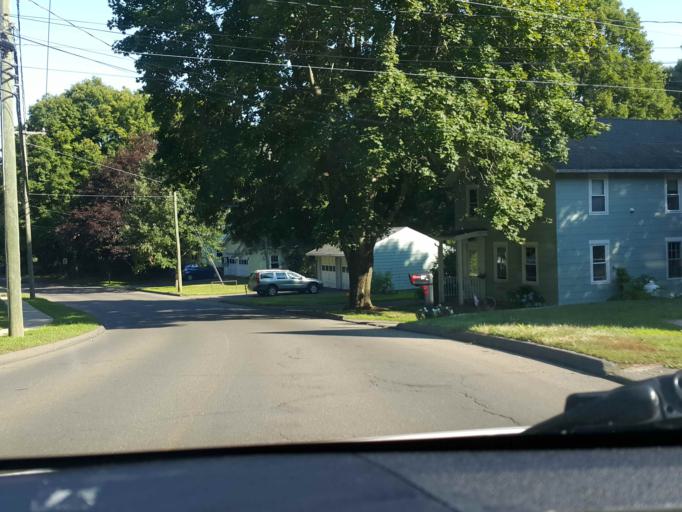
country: US
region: Connecticut
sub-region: New Haven County
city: North Branford
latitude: 41.2729
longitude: -72.7559
